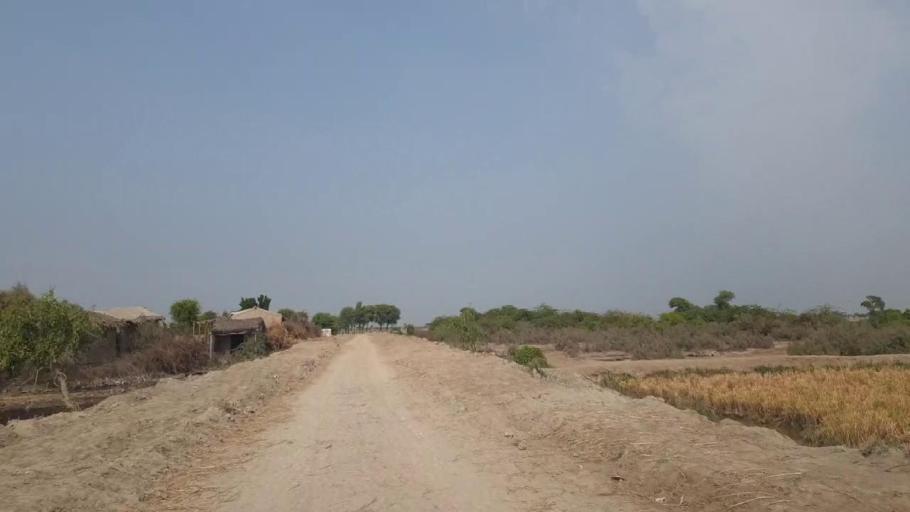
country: PK
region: Sindh
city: Badin
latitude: 24.6167
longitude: 68.7410
